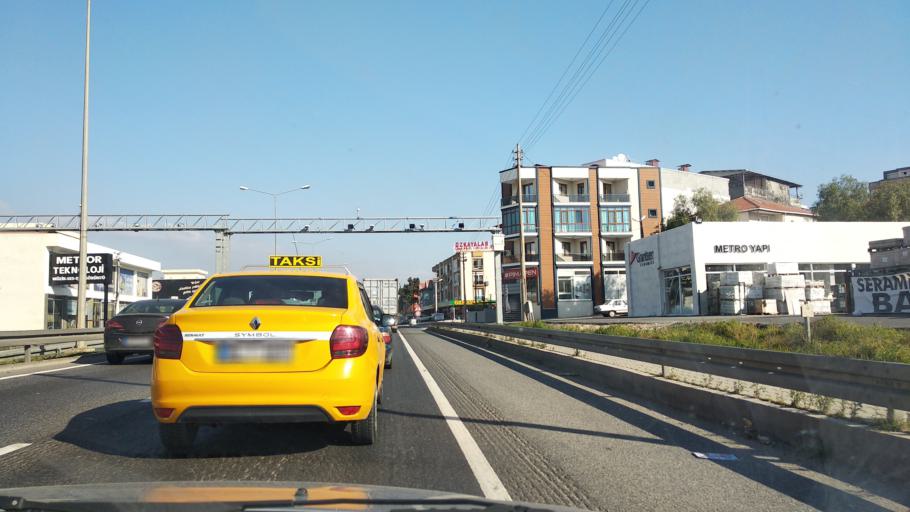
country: TR
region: Izmir
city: Menemen
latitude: 38.5746
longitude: 27.0612
